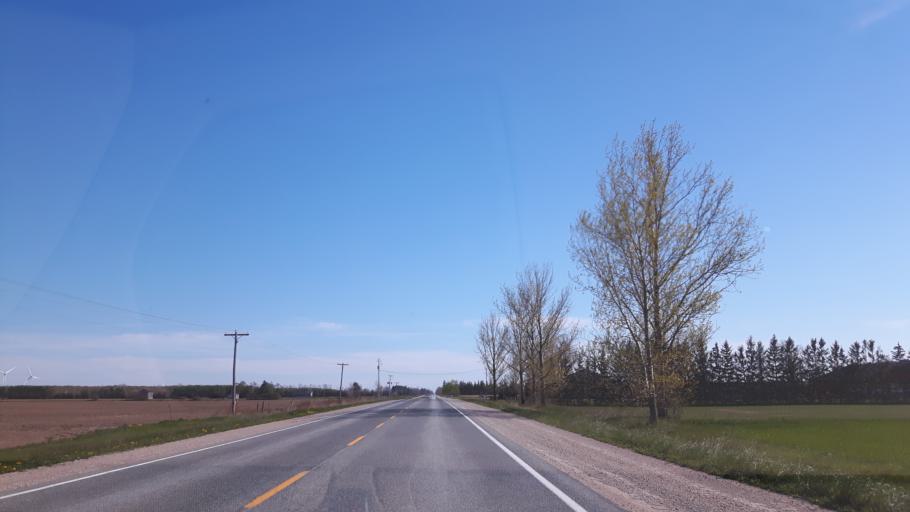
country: CA
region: Ontario
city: Bluewater
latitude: 43.5253
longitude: -81.6926
